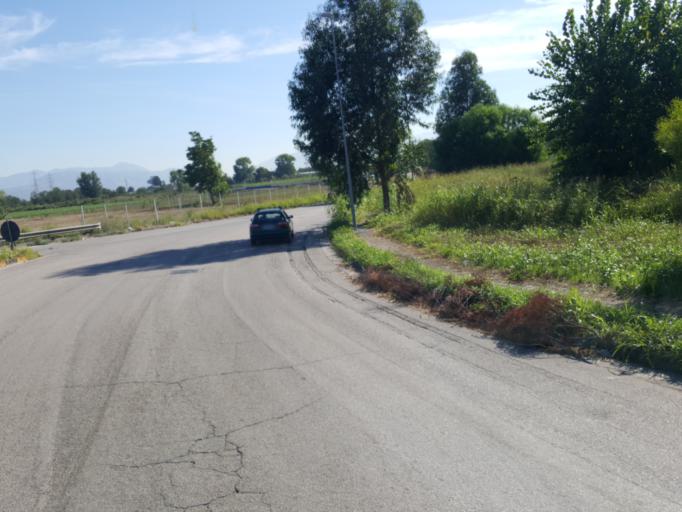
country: IT
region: Campania
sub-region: Provincia di Napoli
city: Pascarola
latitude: 40.9667
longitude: 14.2951
